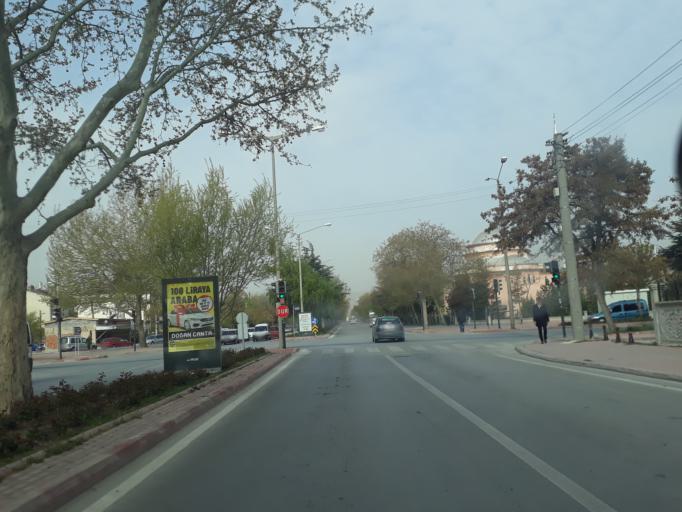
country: TR
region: Konya
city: Selcuklu
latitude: 37.9372
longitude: 32.5099
